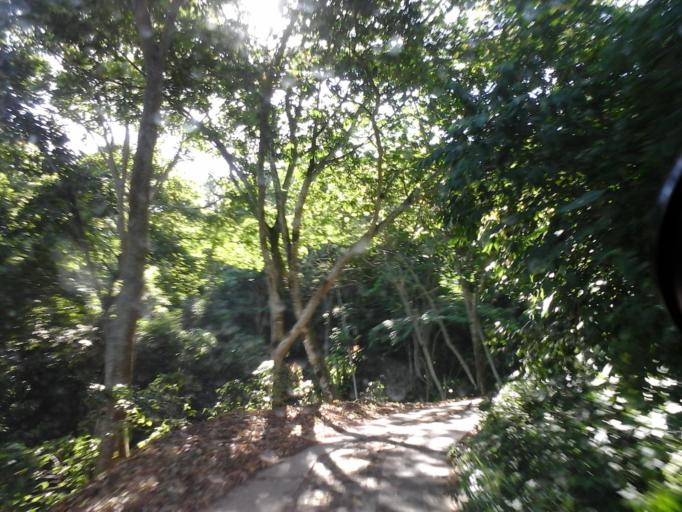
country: CO
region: Cesar
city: San Diego
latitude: 10.2712
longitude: -73.0874
